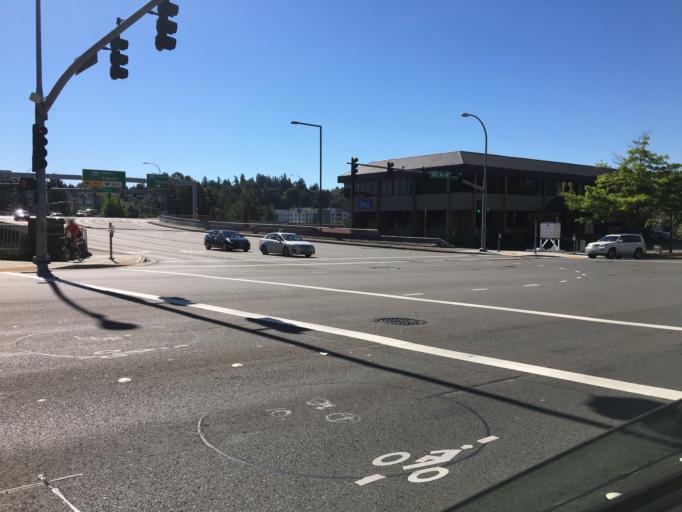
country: US
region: Washington
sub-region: King County
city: Bellevue
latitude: 47.6140
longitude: -122.1909
